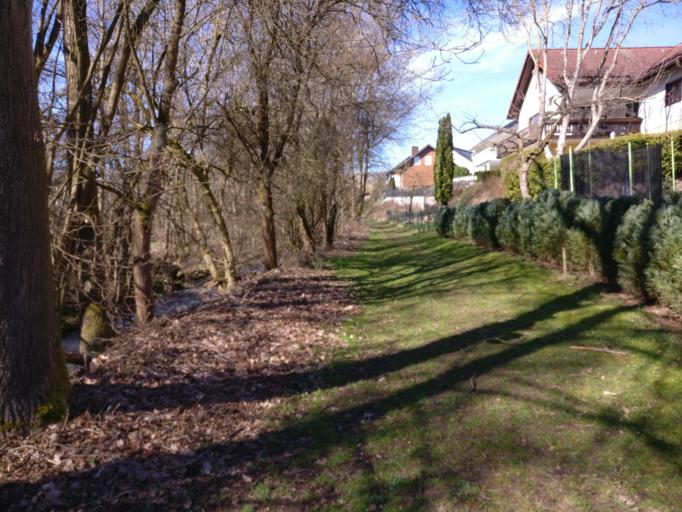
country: DE
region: Hesse
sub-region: Regierungsbezirk Giessen
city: Greifenstein
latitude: 50.6099
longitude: 8.2542
